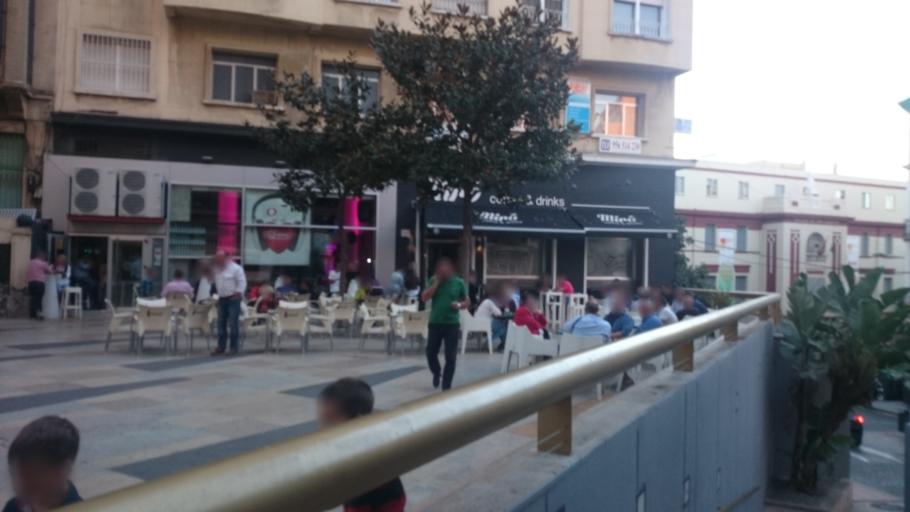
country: ES
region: Ceuta
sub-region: Ceuta
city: Ceuta
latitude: 35.8878
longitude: -5.3104
